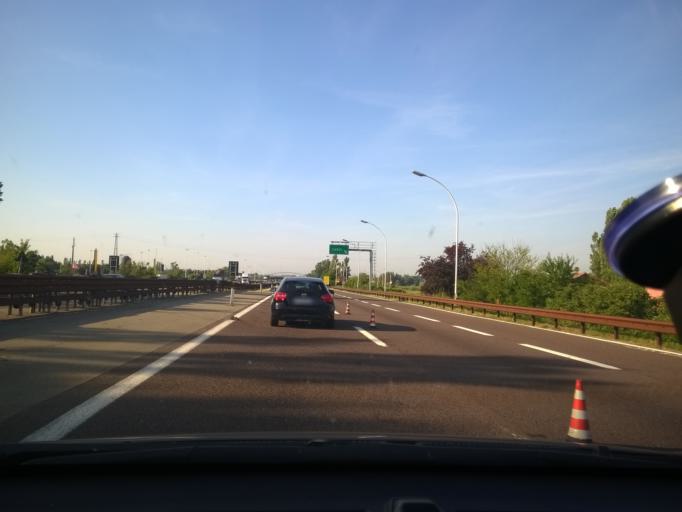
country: IT
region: Emilia-Romagna
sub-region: Provincia di Modena
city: Santa Croce Scuole
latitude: 44.7712
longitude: 10.8451
